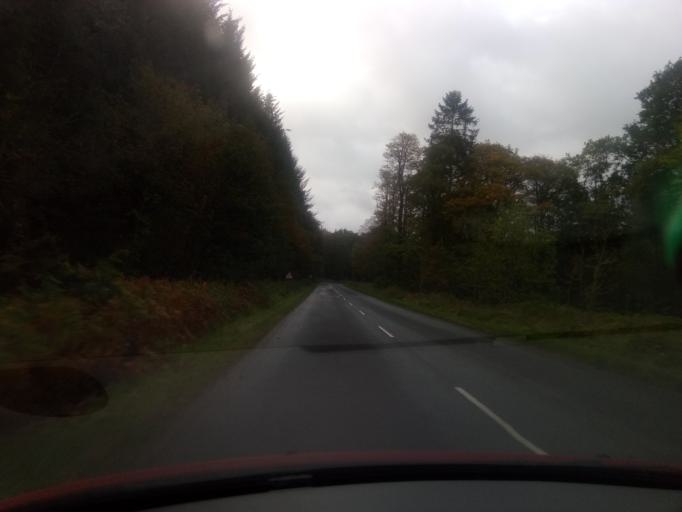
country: GB
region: Scotland
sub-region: The Scottish Borders
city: Hawick
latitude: 55.3504
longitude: -2.6461
